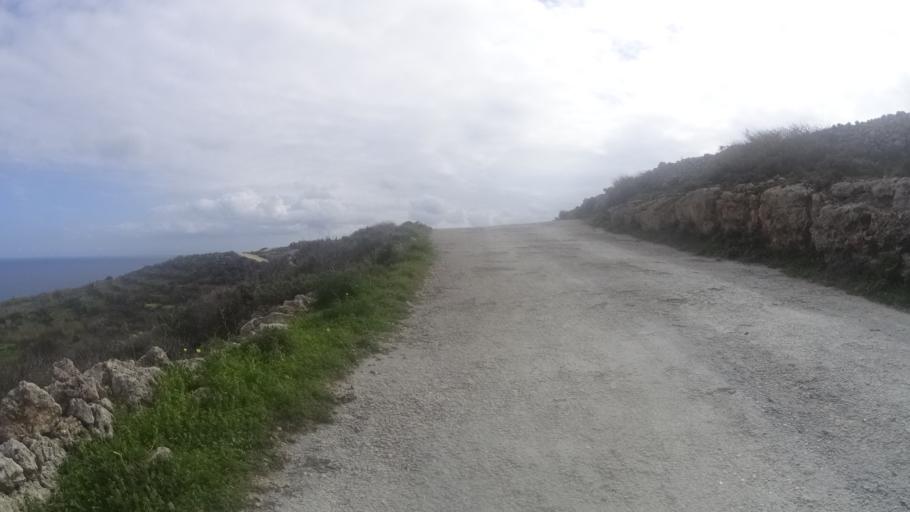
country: MT
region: Il-Qala
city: Qala
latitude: 36.0424
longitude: 14.3177
